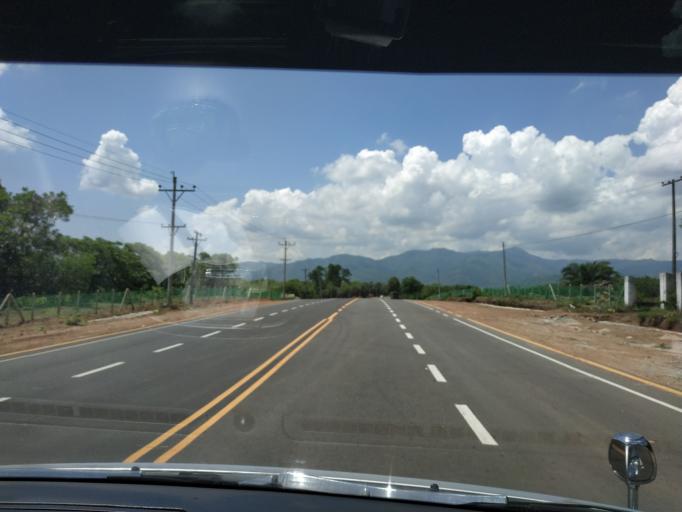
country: MM
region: Mon
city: Kyaikto
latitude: 17.3759
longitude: 97.0527
